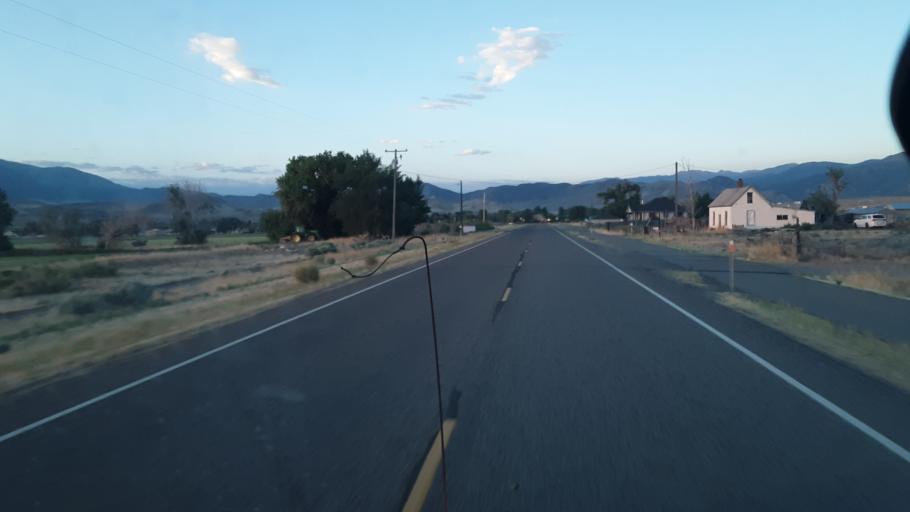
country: US
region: Utah
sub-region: Sevier County
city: Monroe
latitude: 38.6363
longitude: -112.2170
